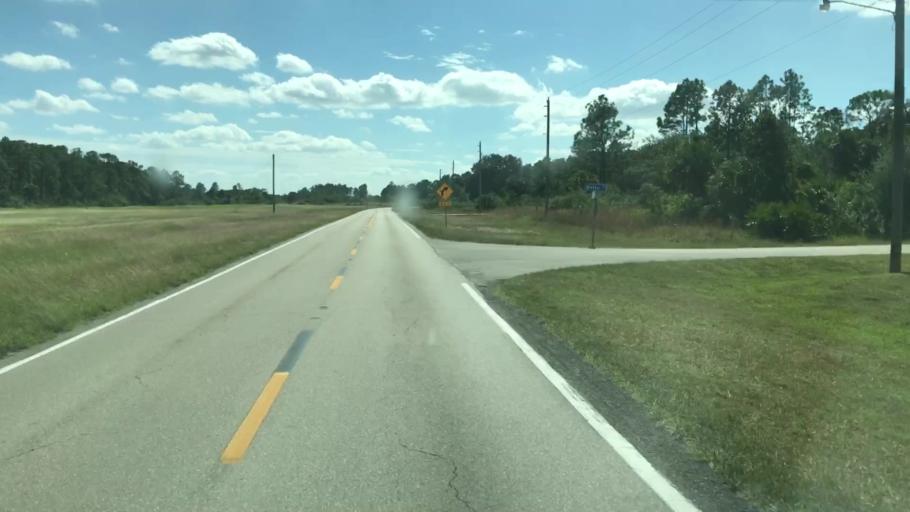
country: US
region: Florida
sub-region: Lee County
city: Lehigh Acres
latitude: 26.6483
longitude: -81.6634
